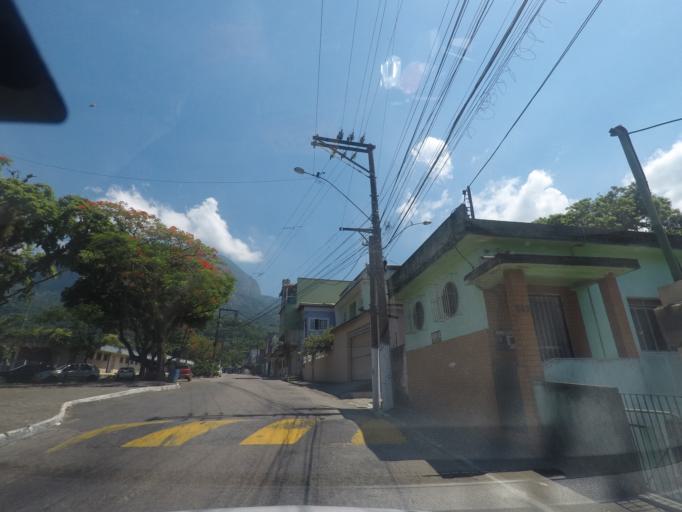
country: BR
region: Rio de Janeiro
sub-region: Petropolis
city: Petropolis
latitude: -22.5714
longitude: -43.1844
